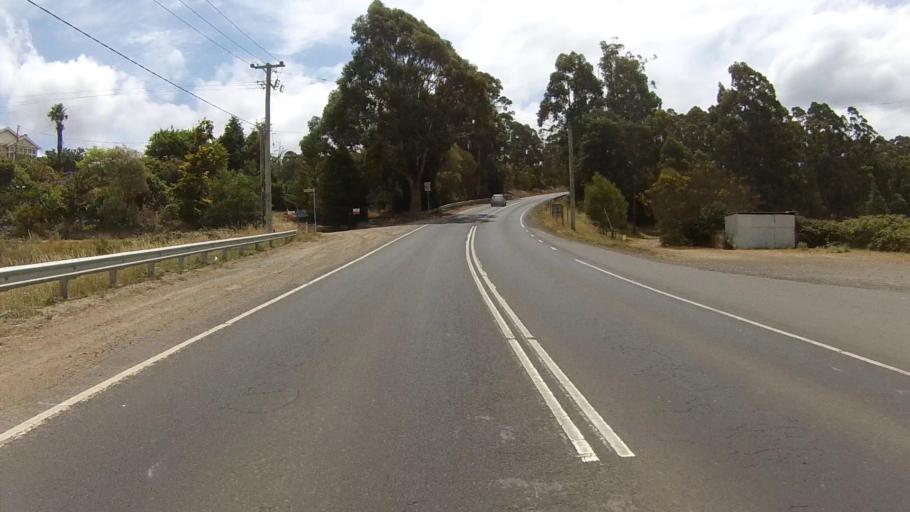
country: AU
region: Tasmania
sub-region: Kingborough
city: Margate
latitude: -43.0637
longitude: 147.2536
